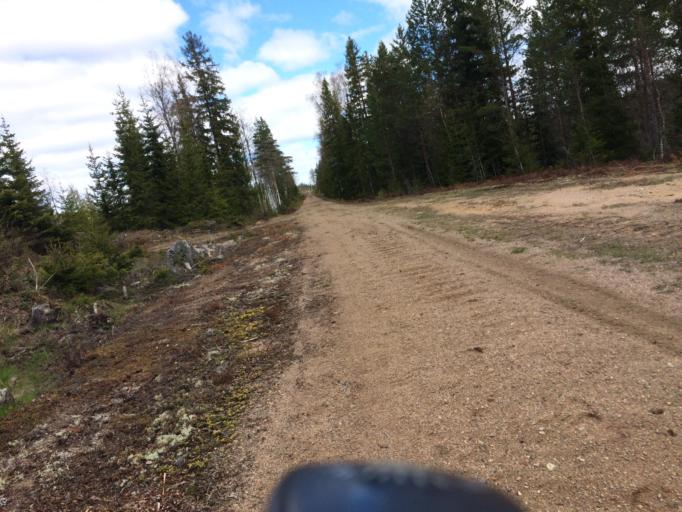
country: SE
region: OErebro
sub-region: Hallefors Kommun
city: Haellefors
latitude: 60.0466
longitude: 14.5270
